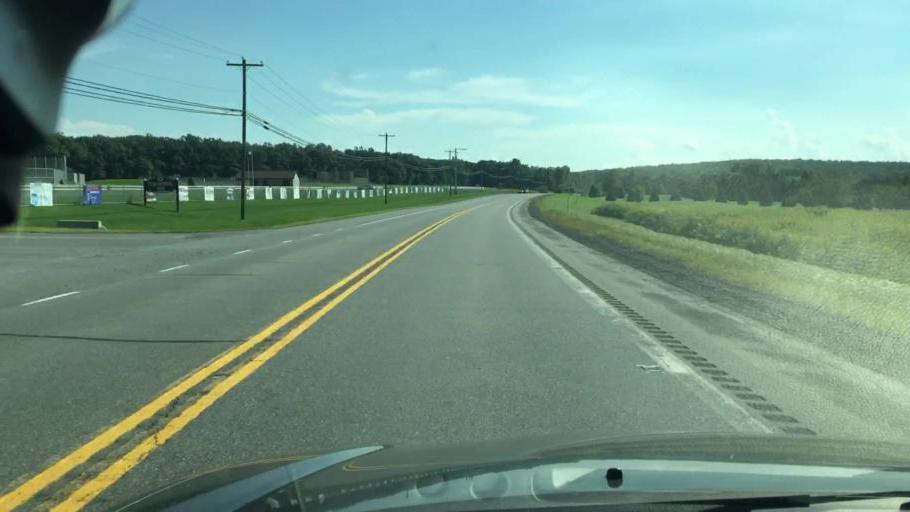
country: US
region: Pennsylvania
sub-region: Carbon County
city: Jim Thorpe
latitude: 40.9335
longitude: -75.6580
